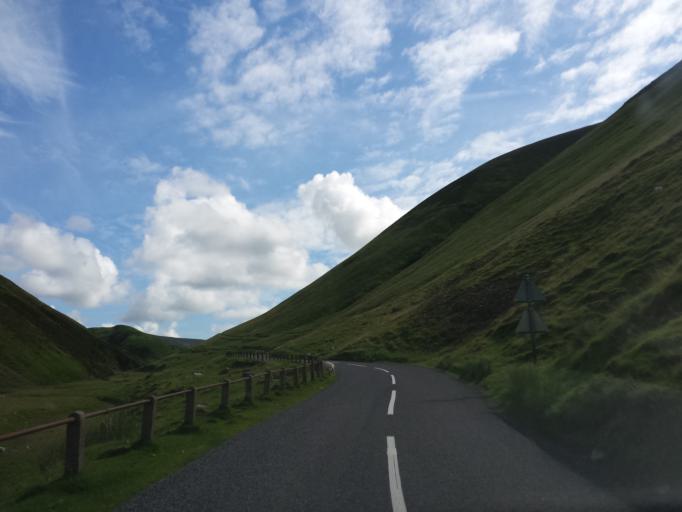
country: GB
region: Scotland
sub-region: Dumfries and Galloway
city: Moffat
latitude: 55.4198
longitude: -3.2822
